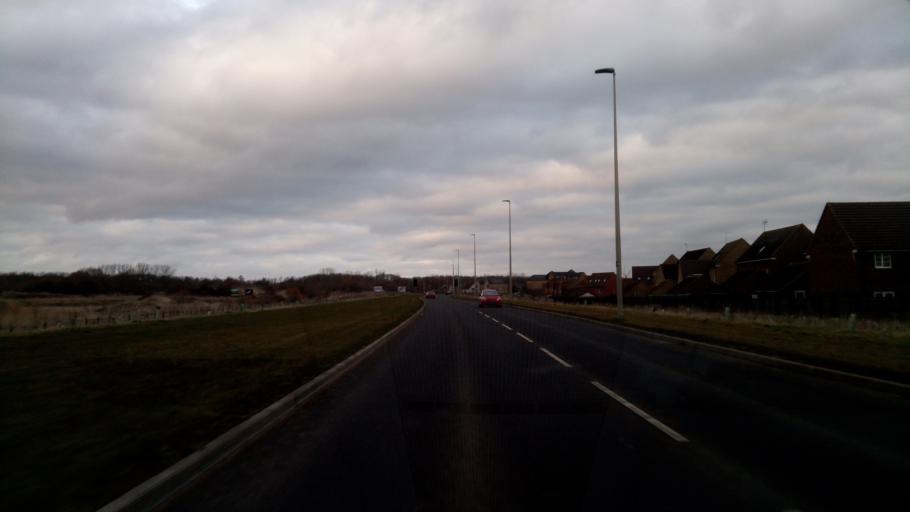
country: GB
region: England
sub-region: Cambridgeshire
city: Yaxley
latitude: 52.5347
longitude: -0.2833
